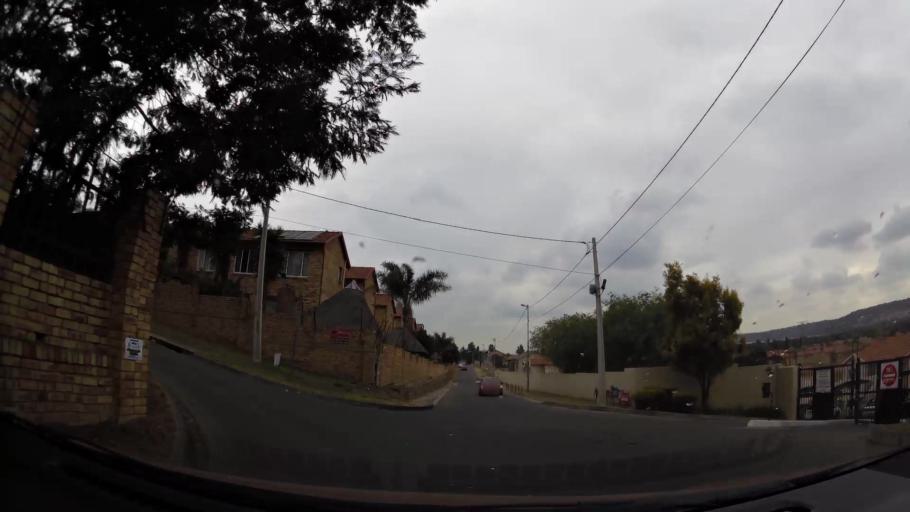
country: ZA
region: Gauteng
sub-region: City of Johannesburg Metropolitan Municipality
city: Roodepoort
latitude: -26.1107
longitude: 27.8995
